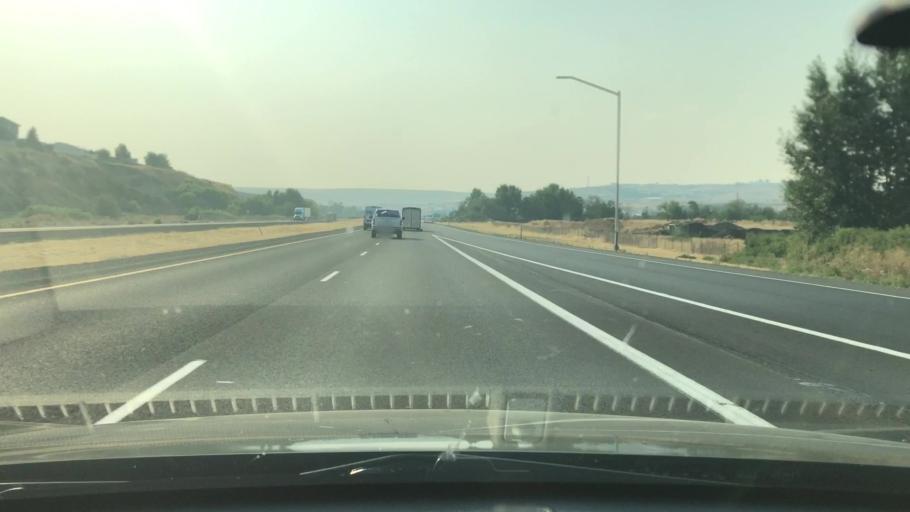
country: US
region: Oregon
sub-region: Umatilla County
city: Pendleton
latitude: 45.6650
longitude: -118.8120
